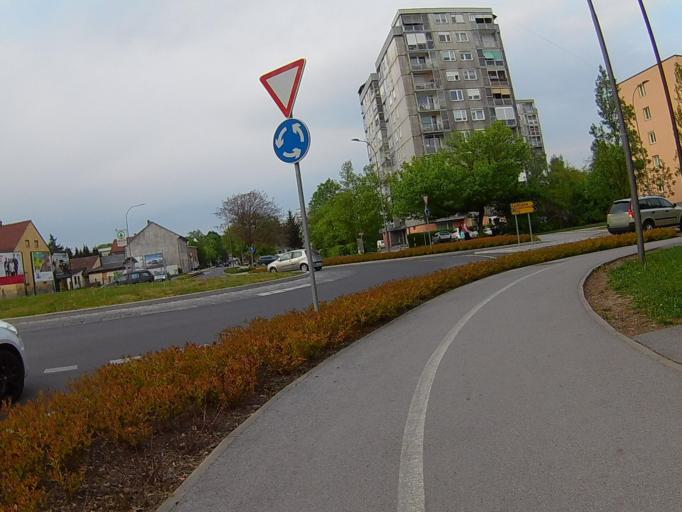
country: SI
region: Maribor
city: Maribor
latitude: 46.5478
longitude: 15.6452
